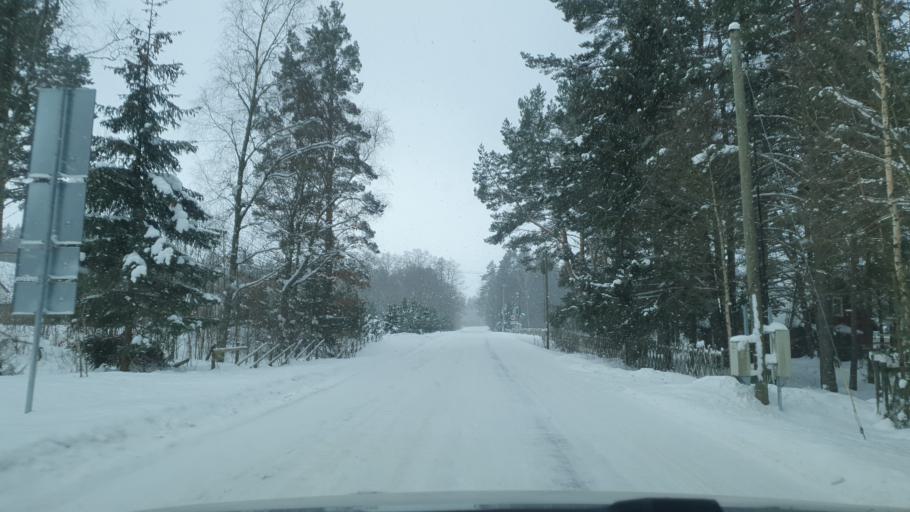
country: EE
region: Harju
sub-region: Kuusalu vald
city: Kuusalu
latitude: 59.4916
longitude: 25.3663
